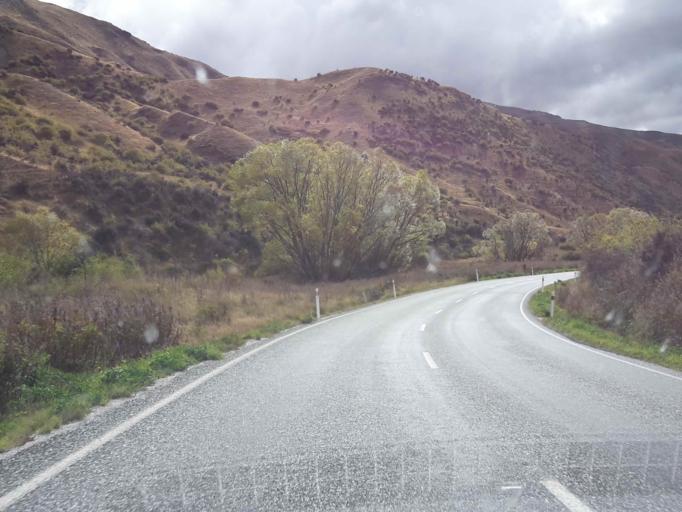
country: NZ
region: Otago
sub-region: Queenstown-Lakes District
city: Arrowtown
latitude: -44.9253
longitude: 168.9712
